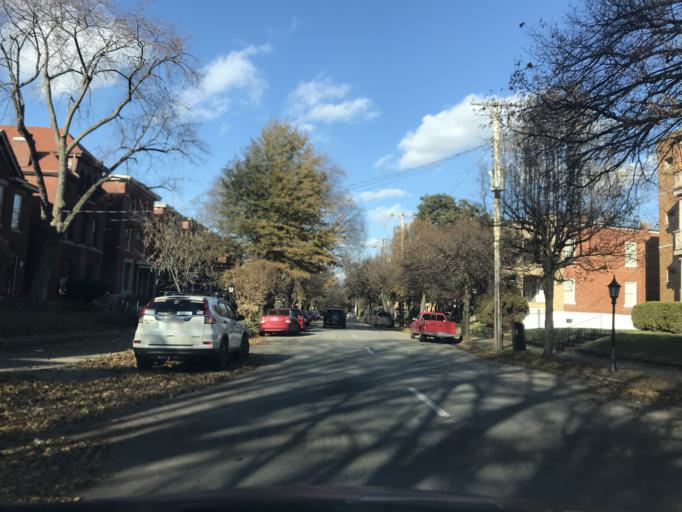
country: US
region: Kentucky
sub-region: Jefferson County
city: Louisville
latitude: 38.2277
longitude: -85.7583
